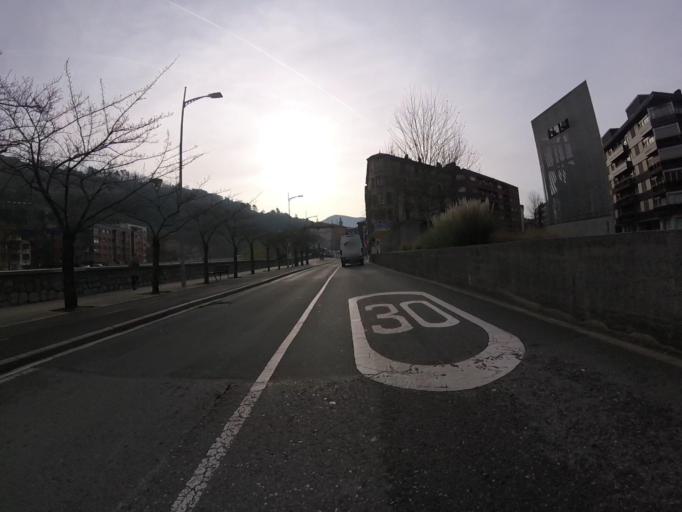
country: ES
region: Basque Country
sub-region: Provincia de Guipuzcoa
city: Tolosa
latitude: 43.1413
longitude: -2.0726
